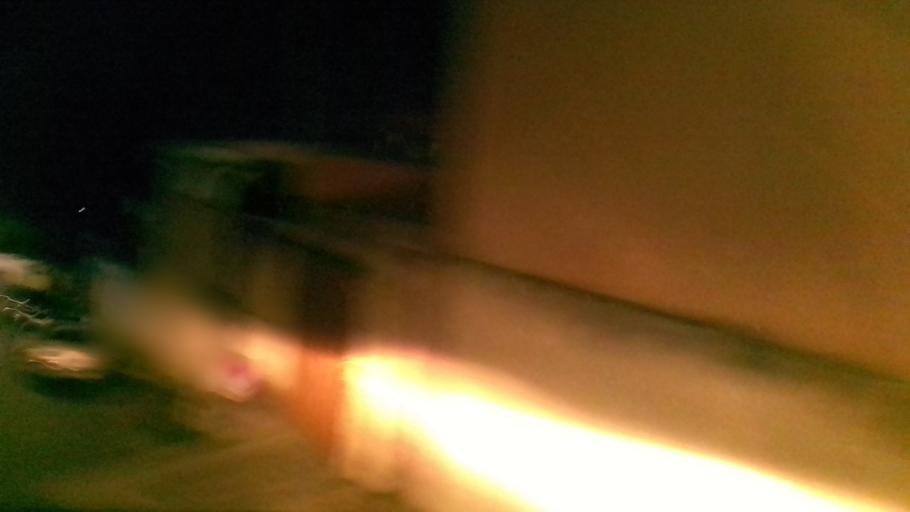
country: BR
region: Minas Gerais
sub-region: Belo Horizonte
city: Belo Horizonte
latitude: -19.9017
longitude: -43.9622
